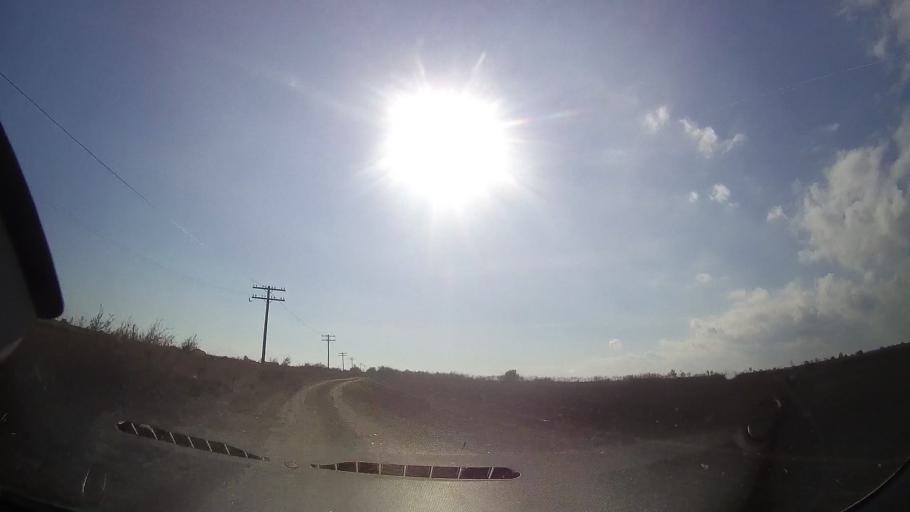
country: RO
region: Constanta
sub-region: Comuna Tuzla
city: Tuzla
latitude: 43.9768
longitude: 28.6442
